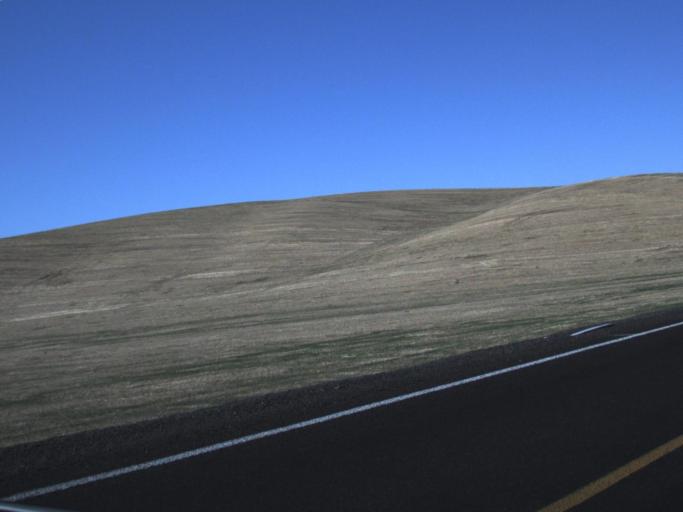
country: US
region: Washington
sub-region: Walla Walla County
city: Walla Walla
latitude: 46.1041
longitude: -118.3728
